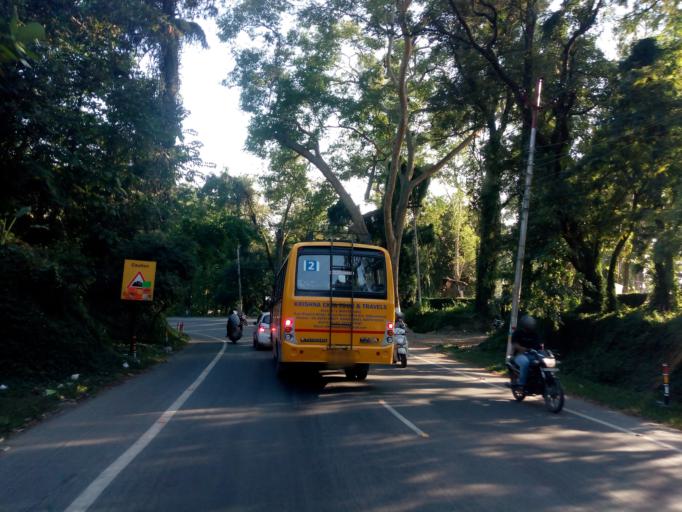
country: IN
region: Uttarakhand
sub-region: Dehradun
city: Dehradun
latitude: 30.3511
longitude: 78.0435
